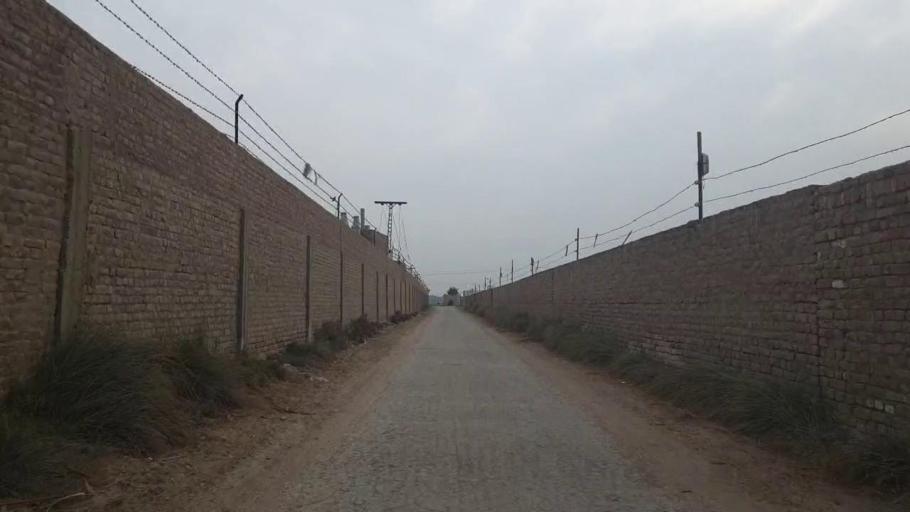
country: PK
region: Sindh
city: Shahdadpur
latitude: 25.9354
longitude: 68.7014
